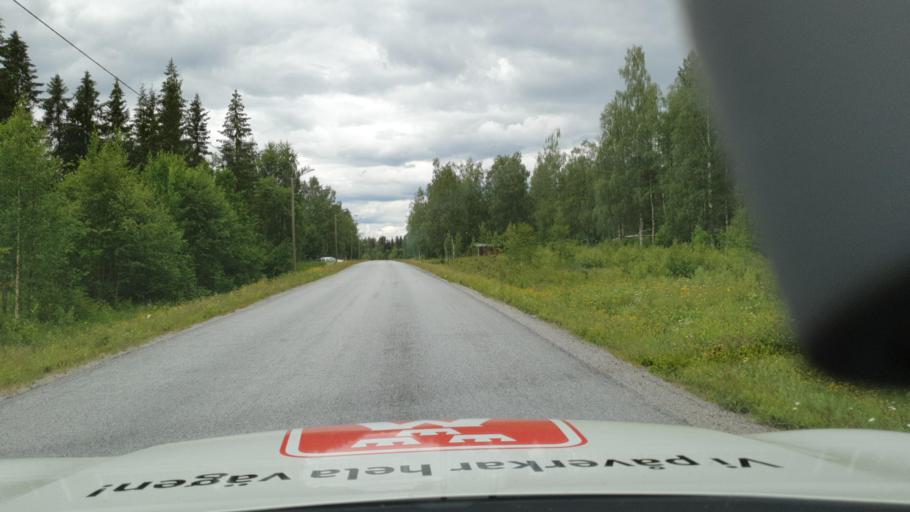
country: SE
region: Vaesterbotten
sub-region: Bjurholms Kommun
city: Bjurholm
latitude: 63.7830
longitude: 19.2098
